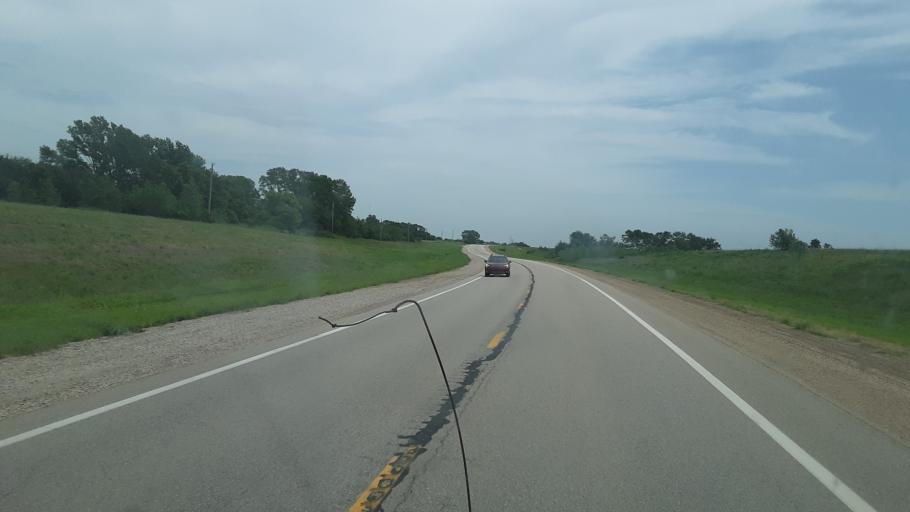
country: US
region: Kansas
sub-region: Woodson County
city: Yates Center
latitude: 37.8360
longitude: -95.8697
